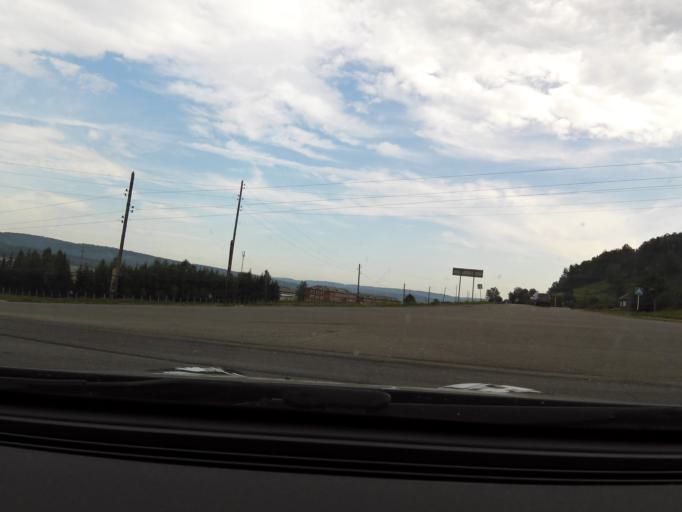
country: RU
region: Chelyabinsk
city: Sim
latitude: 55.0057
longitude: 57.7069
